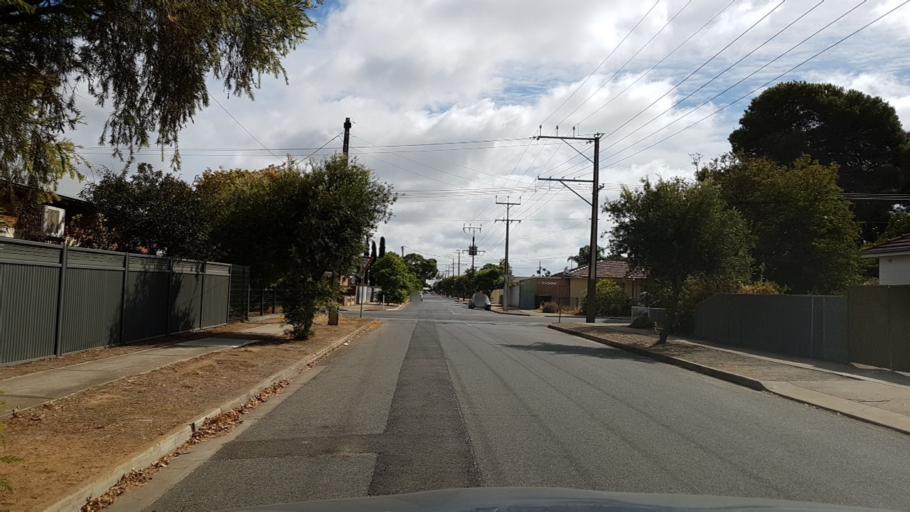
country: AU
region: South Australia
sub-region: Marion
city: Plympton Park
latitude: -34.9878
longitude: 138.5502
